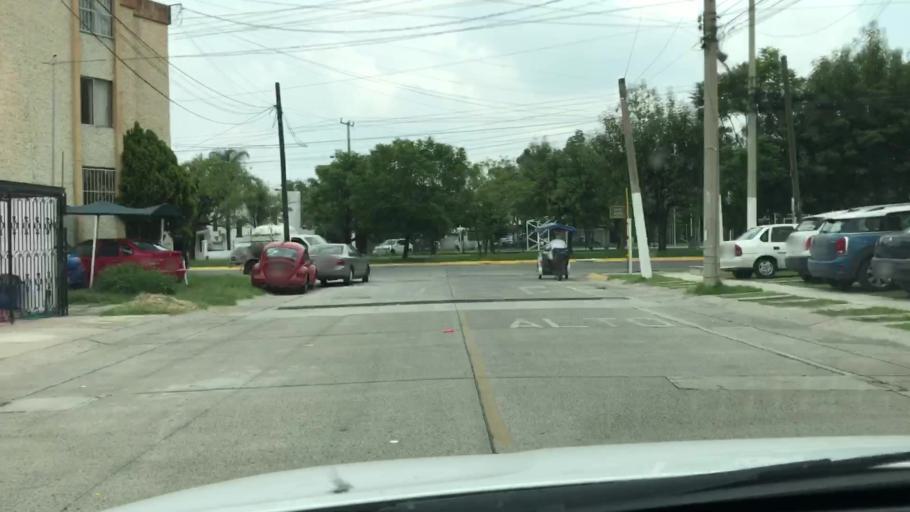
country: MX
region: Jalisco
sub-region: Tlajomulco de Zuniga
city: Palomar
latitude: 20.6360
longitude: -103.4331
